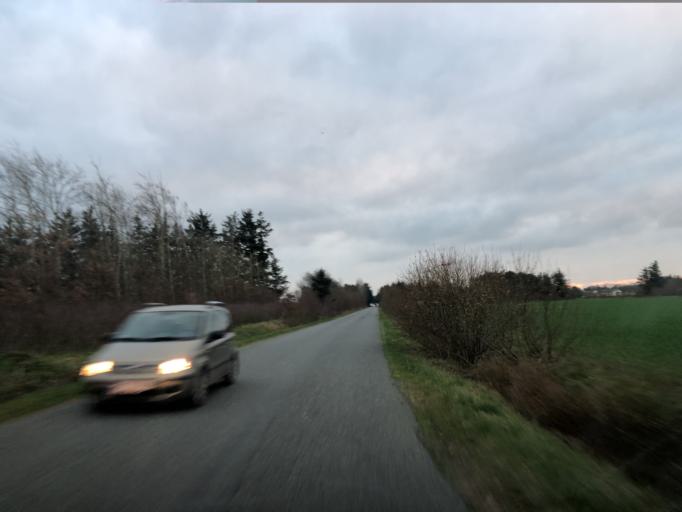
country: DK
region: Central Jutland
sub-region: Holstebro Kommune
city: Ulfborg
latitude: 56.2626
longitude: 8.2852
